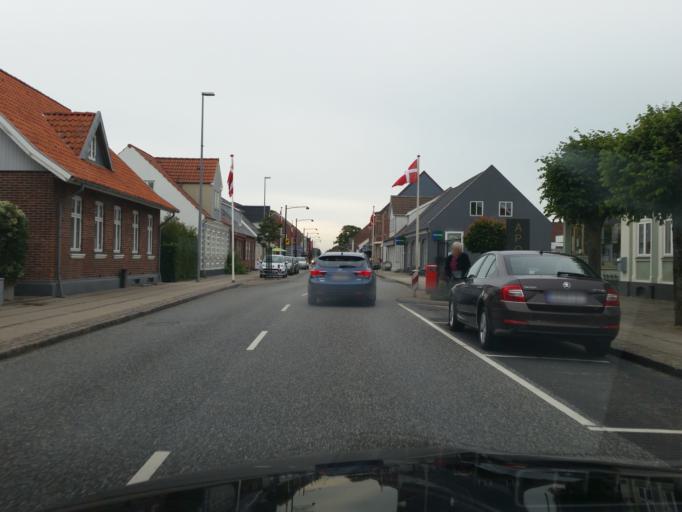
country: DK
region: South Denmark
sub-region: Varde Kommune
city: Oksbol
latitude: 55.7798
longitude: 8.2864
